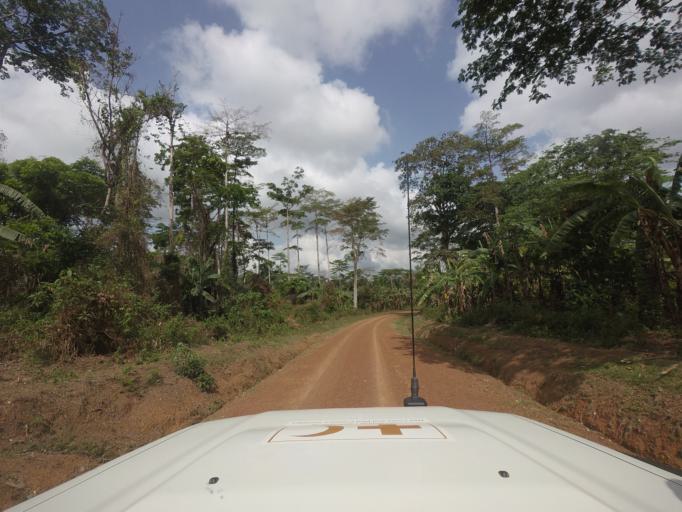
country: LR
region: Bong
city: Gbarnga
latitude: 7.1742
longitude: -9.0876
